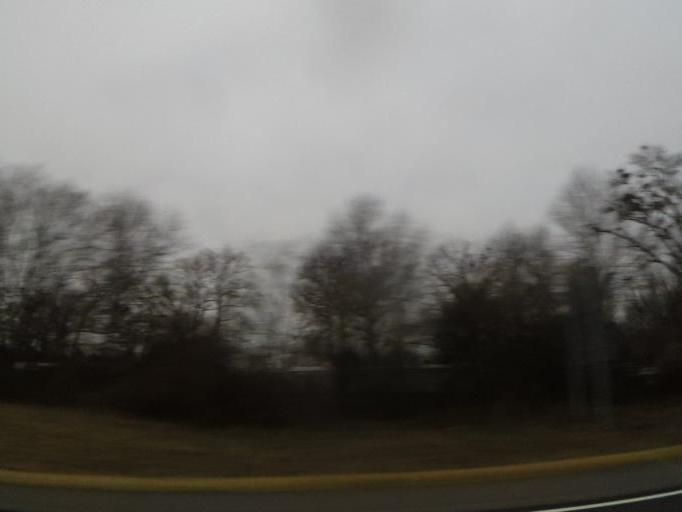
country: US
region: Alabama
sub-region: Cullman County
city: Good Hope
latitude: 34.1449
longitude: -86.8693
